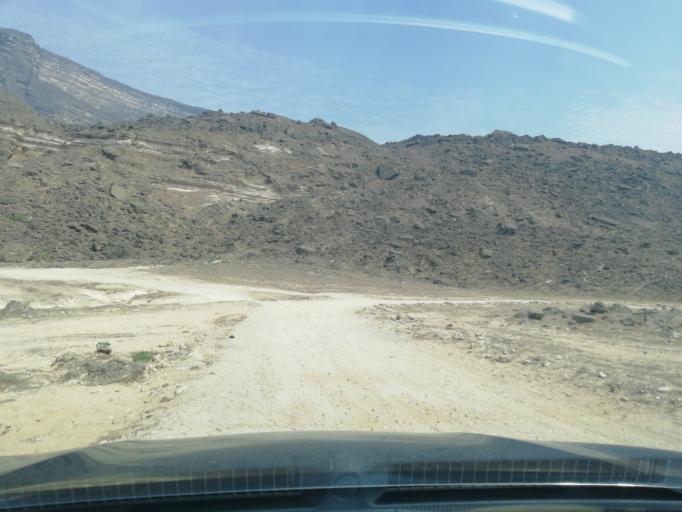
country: OM
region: Zufar
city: Salalah
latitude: 16.8164
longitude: 53.6900
